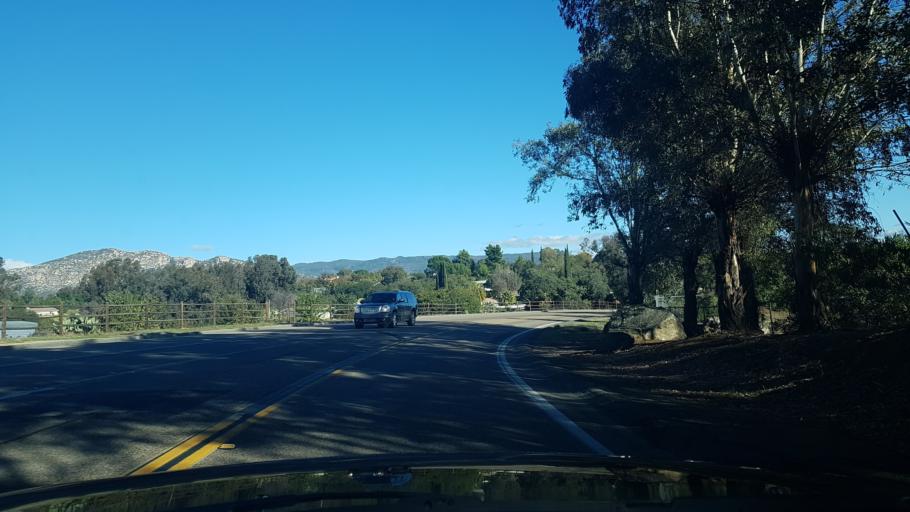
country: US
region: California
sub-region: San Diego County
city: Valley Center
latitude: 33.2077
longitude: -116.9515
